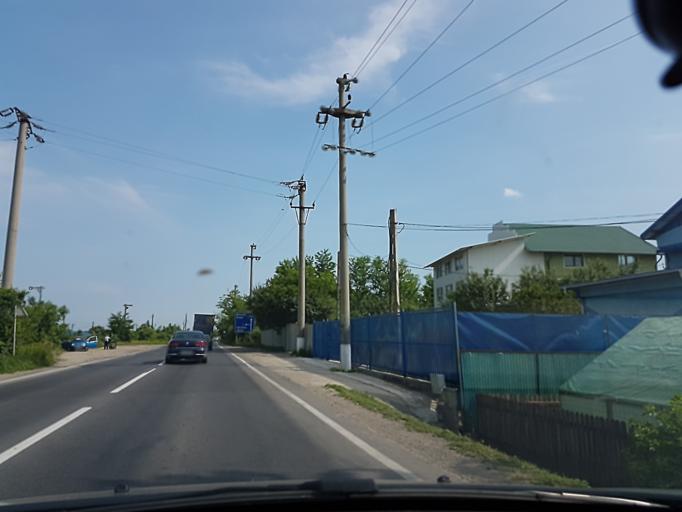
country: RO
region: Prahova
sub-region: Comuna Blejoiu
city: Blejoi
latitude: 44.9913
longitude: 26.0139
